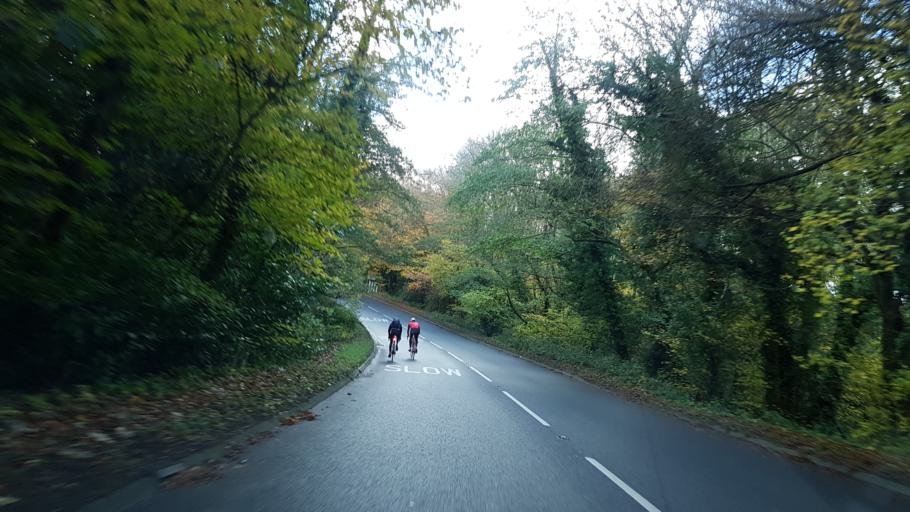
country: GB
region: England
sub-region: Surrey
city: Haslemere
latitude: 51.1068
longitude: -0.6894
